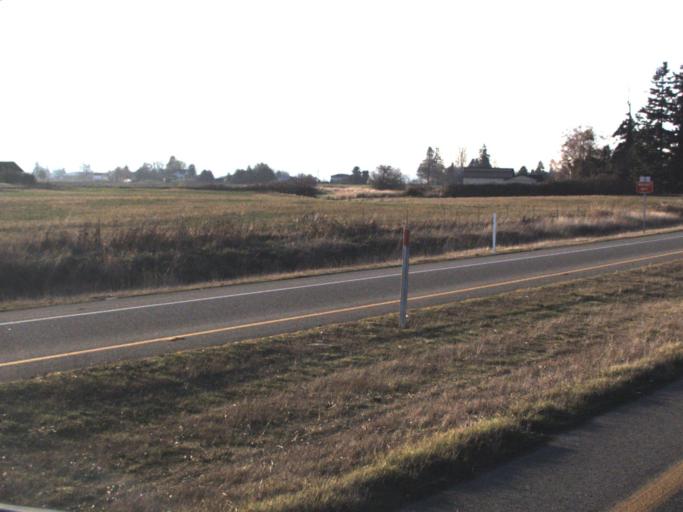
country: US
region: Washington
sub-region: Skagit County
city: Mount Vernon
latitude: 48.4450
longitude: -122.4290
